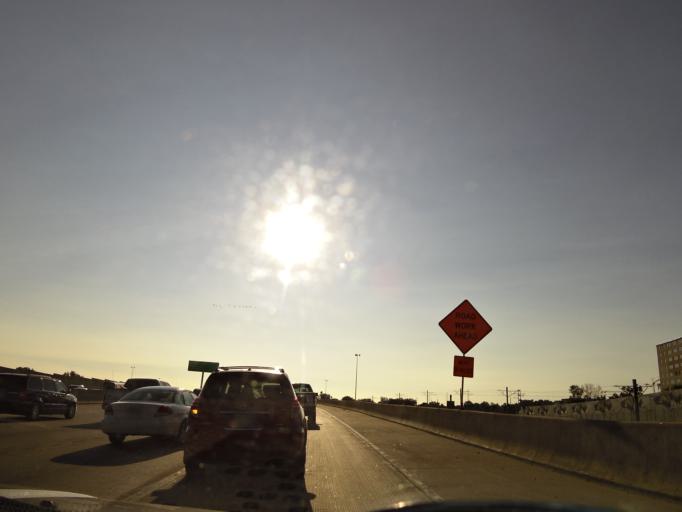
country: US
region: Colorado
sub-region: Arapahoe County
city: Glendale
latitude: 39.6852
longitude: -104.9634
